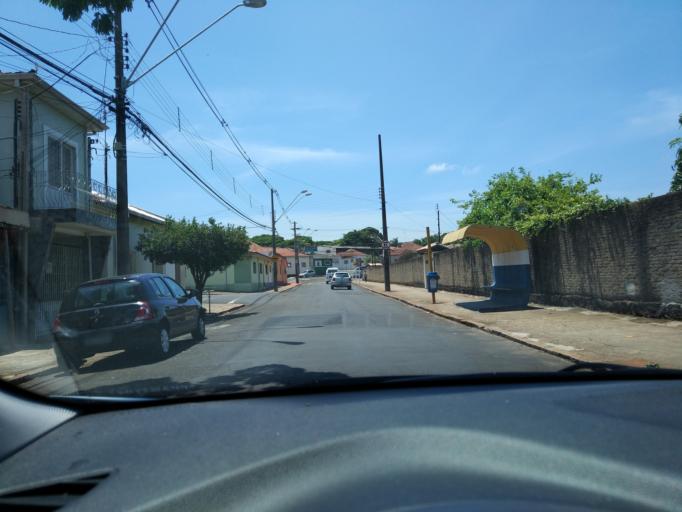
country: BR
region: Sao Paulo
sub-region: Botucatu
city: Botucatu
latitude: -22.8723
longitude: -48.4449
